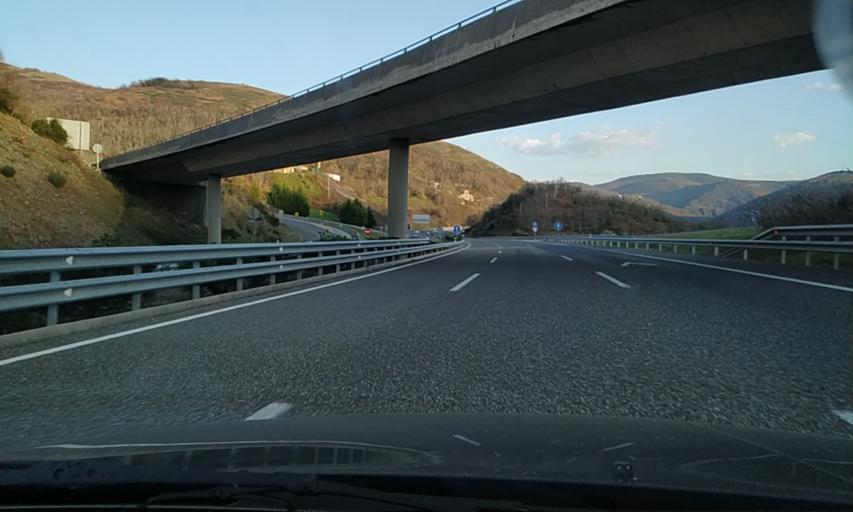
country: ES
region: Galicia
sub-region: Provincia de Lugo
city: San Roman
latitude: 42.7650
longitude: -7.0845
